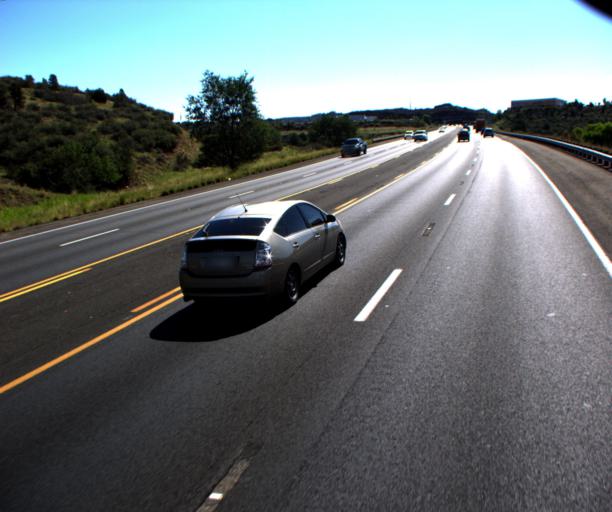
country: US
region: Arizona
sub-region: Yavapai County
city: Prescott
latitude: 34.5524
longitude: -112.4189
